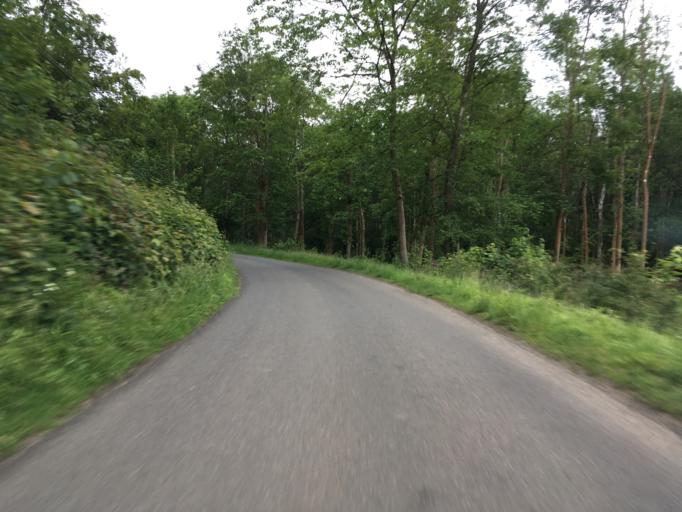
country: GB
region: England
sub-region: Wiltshire
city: Luckington
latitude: 51.5745
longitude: -2.2864
